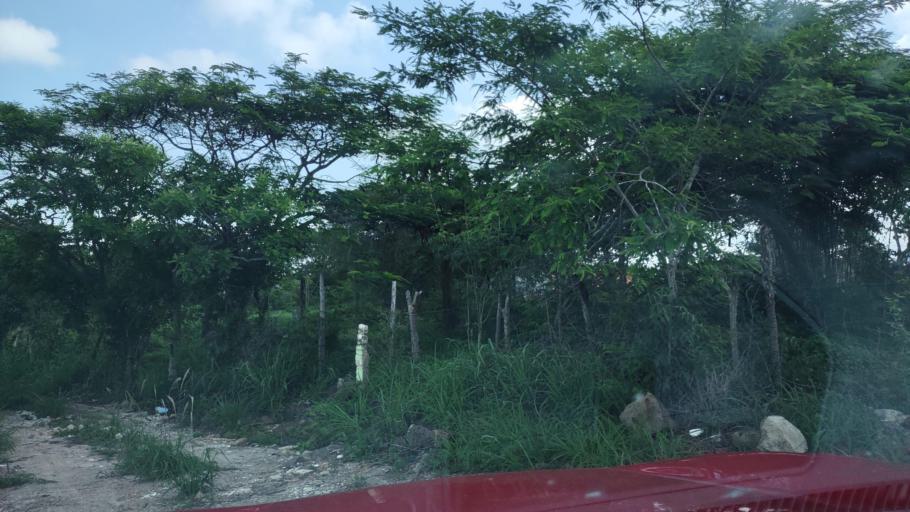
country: MX
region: Veracruz
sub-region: Emiliano Zapata
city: Dos Rios
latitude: 19.4494
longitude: -96.8104
